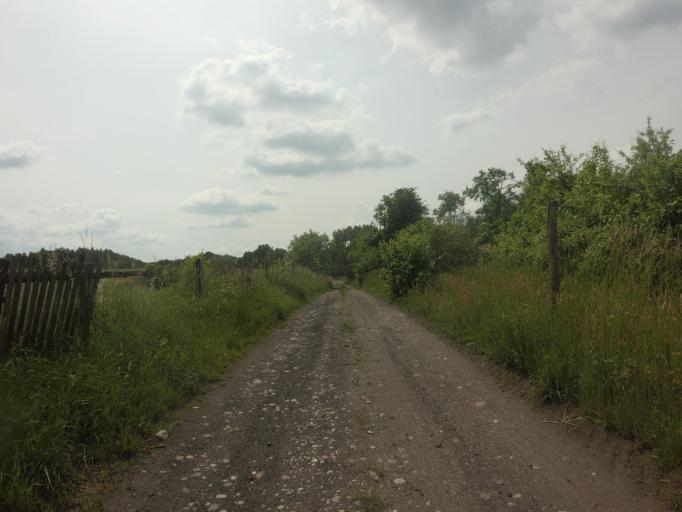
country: PL
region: West Pomeranian Voivodeship
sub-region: Powiat stargardzki
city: Dobrzany
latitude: 53.3222
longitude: 15.4927
